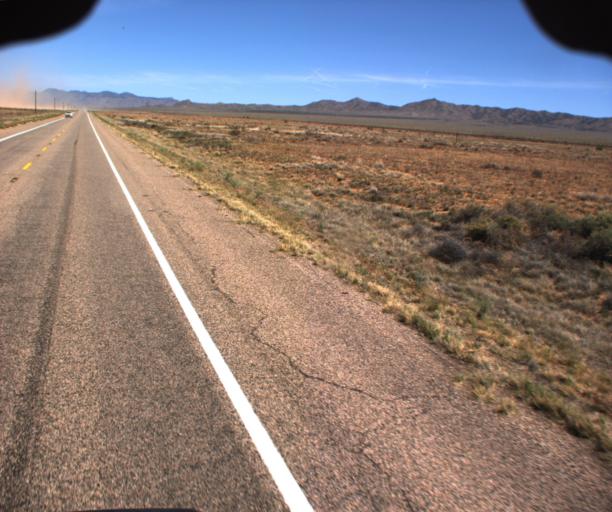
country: US
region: Arizona
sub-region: Mohave County
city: New Kingman-Butler
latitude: 35.3382
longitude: -113.8950
